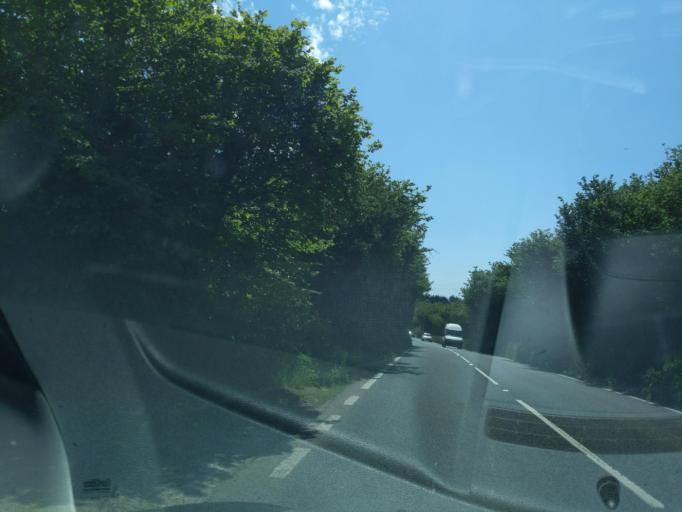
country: GB
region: England
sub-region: Cornwall
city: Camelford
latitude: 50.6045
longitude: -4.6938
